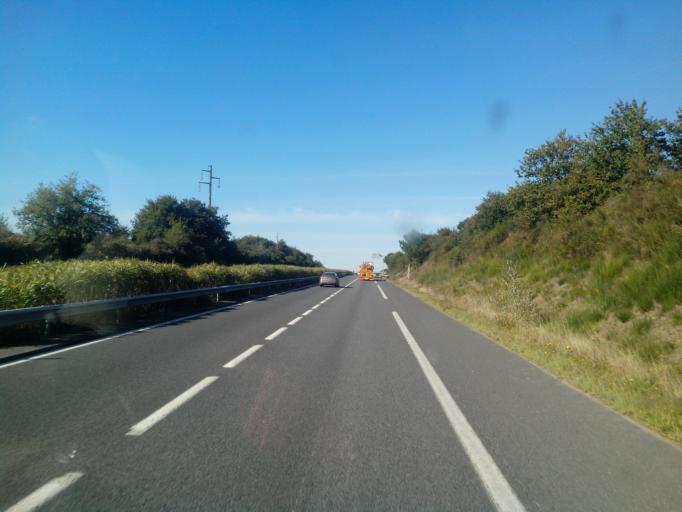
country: FR
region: Brittany
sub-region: Departement du Morbihan
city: Nivillac
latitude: 47.5157
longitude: -2.2776
